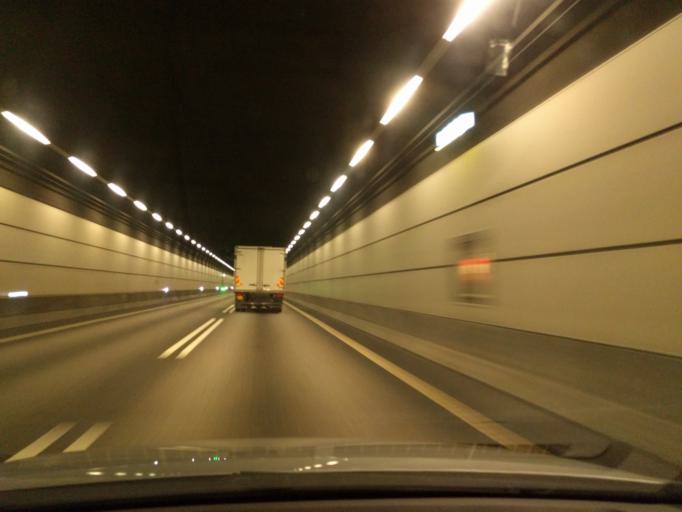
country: DK
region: Capital Region
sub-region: Dragor Kommune
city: Dragor
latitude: 55.6198
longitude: 12.7050
